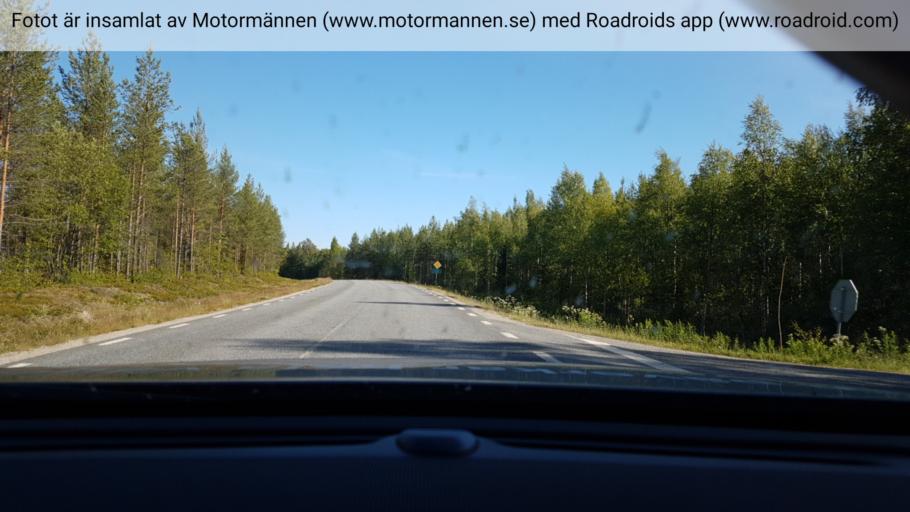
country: SE
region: Vaesterbotten
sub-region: Lycksele Kommun
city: Lycksele
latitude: 64.4602
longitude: 18.9040
